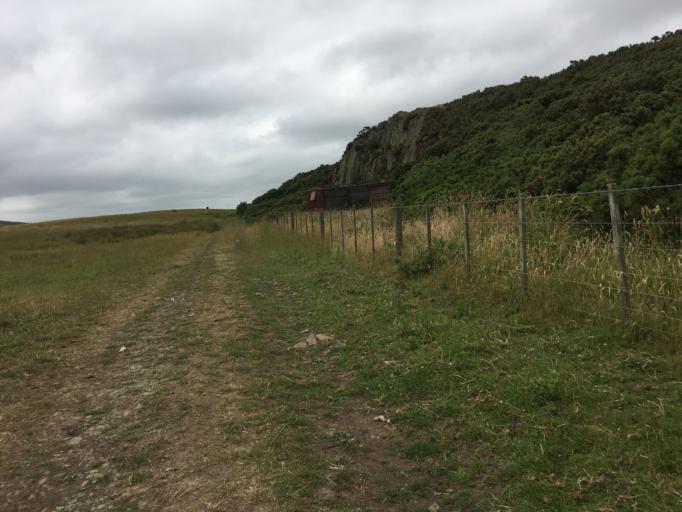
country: GB
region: England
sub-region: Northumberland
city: Belford
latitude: 55.6129
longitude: -1.8915
